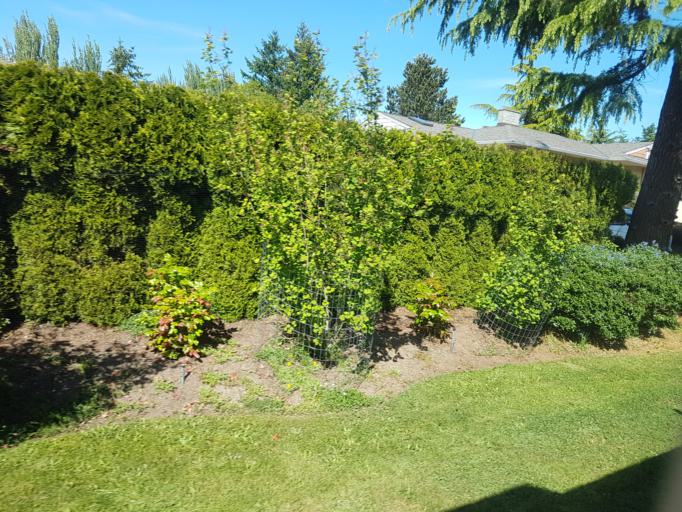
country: CA
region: British Columbia
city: Oak Bay
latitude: 48.4899
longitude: -123.3200
